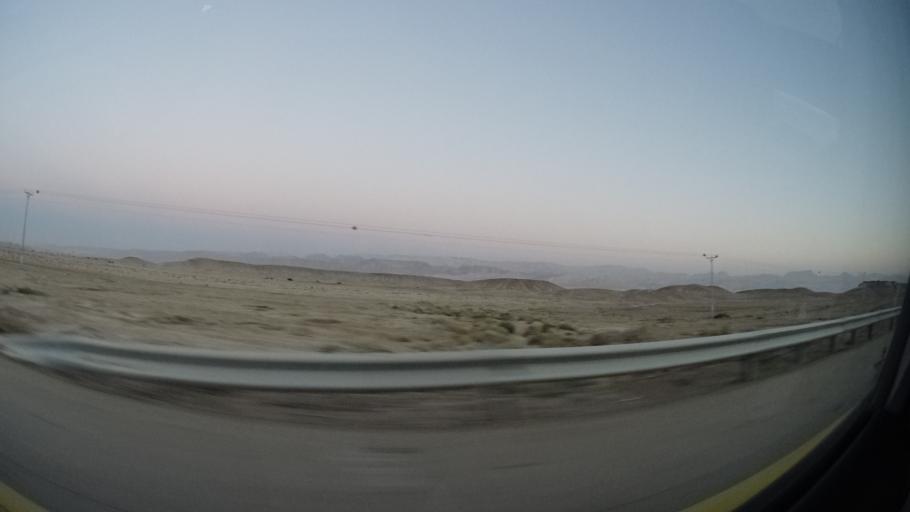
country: JO
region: Ma'an
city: At Tayyibah
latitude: 30.1184
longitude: 35.1456
